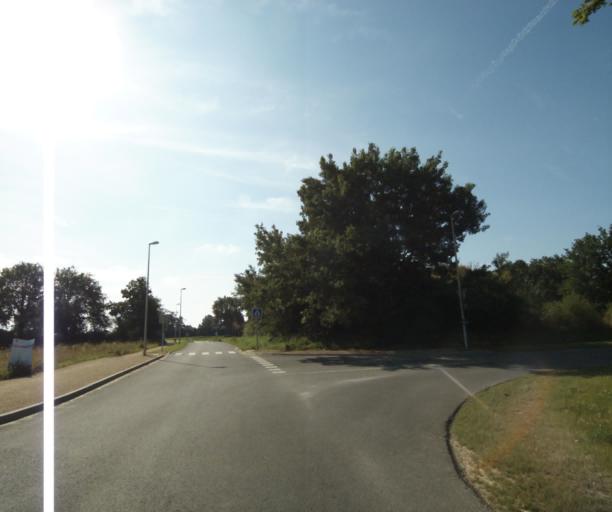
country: FR
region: Pays de la Loire
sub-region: Departement de la Mayenne
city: Laval
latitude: 48.0537
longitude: -0.7854
